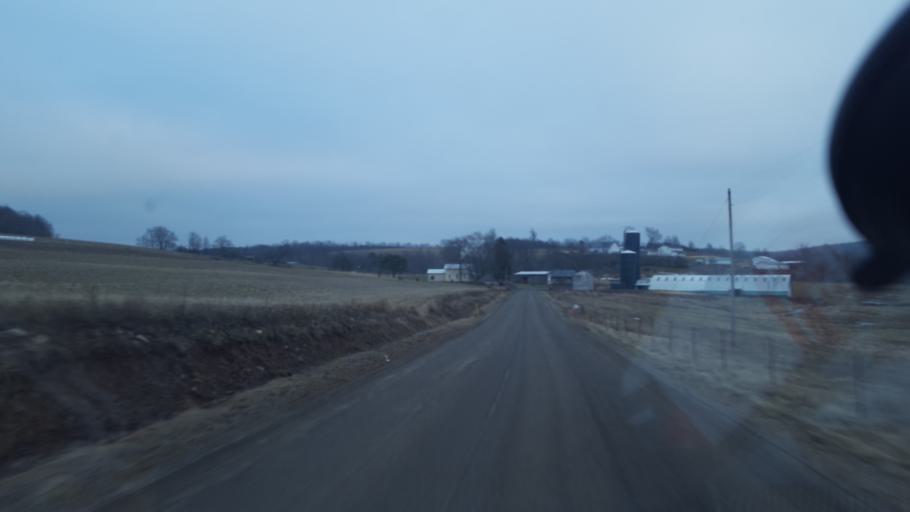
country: US
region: Pennsylvania
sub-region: Tioga County
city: Westfield
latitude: 41.9247
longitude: -77.7624
